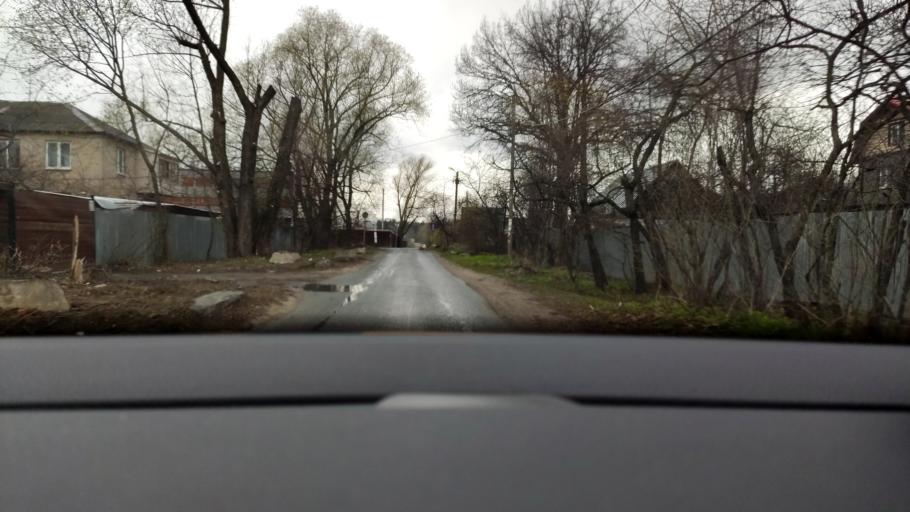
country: RU
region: Moskovskaya
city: Reutov
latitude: 55.7735
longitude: 37.8869
